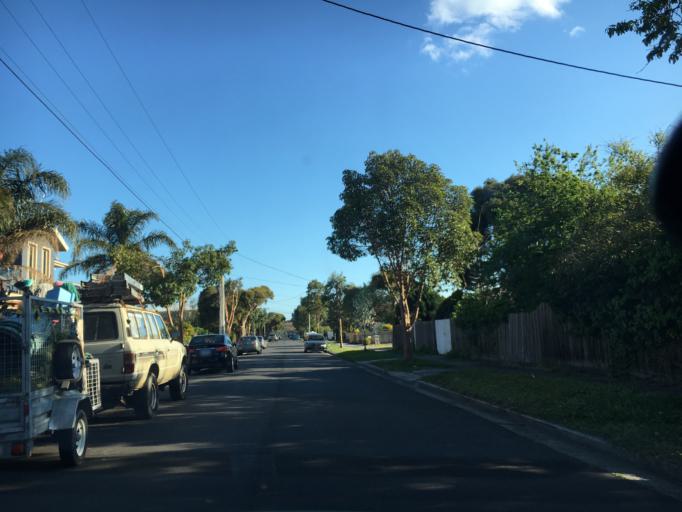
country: AU
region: Victoria
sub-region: Kingston
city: Clayton South
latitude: -37.9323
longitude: 145.1253
